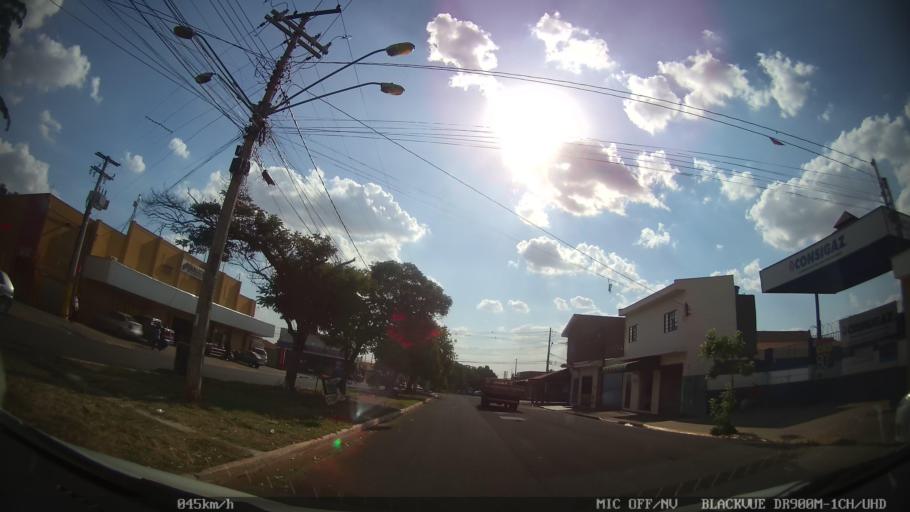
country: BR
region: Sao Paulo
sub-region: Ribeirao Preto
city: Ribeirao Preto
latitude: -21.2019
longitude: -47.8436
